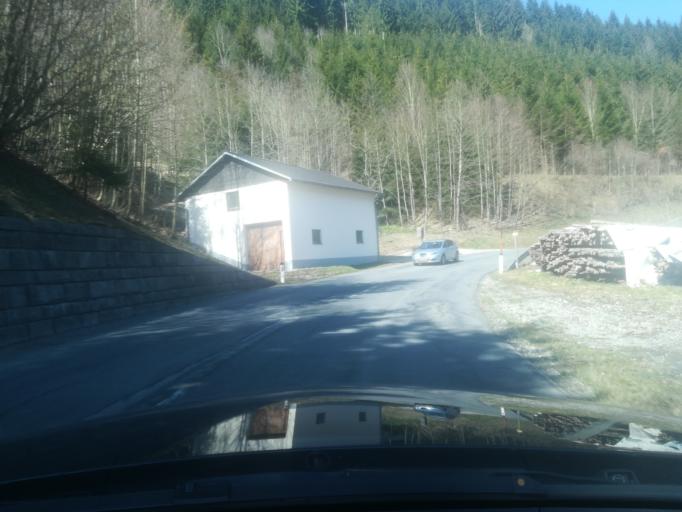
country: AT
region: Upper Austria
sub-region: Politischer Bezirk Perg
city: Sankt Georgen am Walde
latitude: 48.4465
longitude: 14.7820
